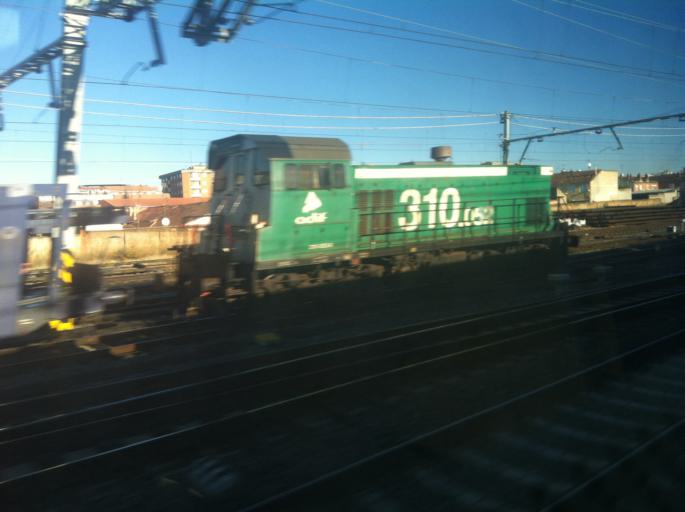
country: ES
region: Castille and Leon
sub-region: Provincia de Palencia
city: Venta de Banos
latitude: 41.9187
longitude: -4.4950
